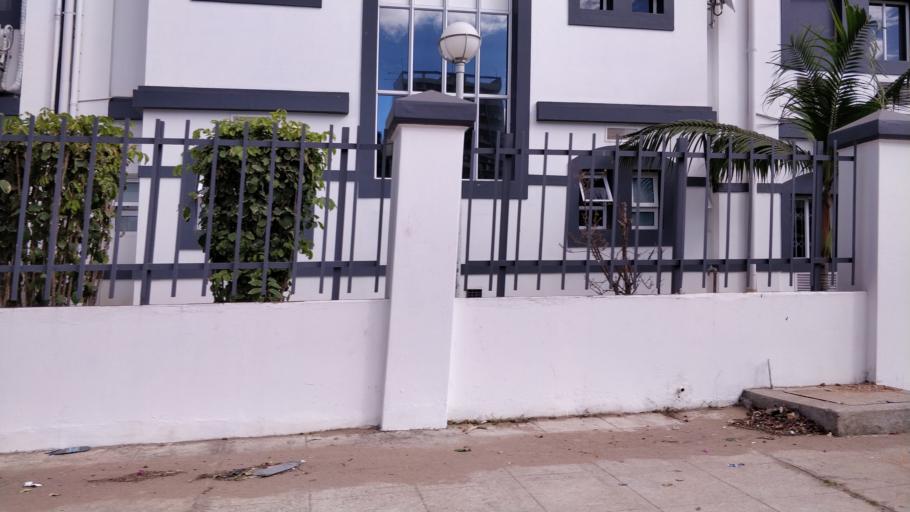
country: MZ
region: Maputo City
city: Maputo
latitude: -25.9769
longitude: 32.5761
